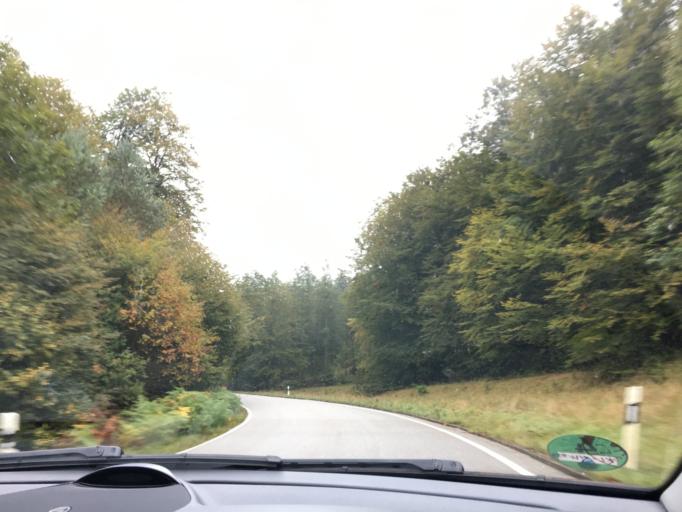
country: DE
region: Rheinland-Pfalz
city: Schmalenberg
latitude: 49.3432
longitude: 7.7340
